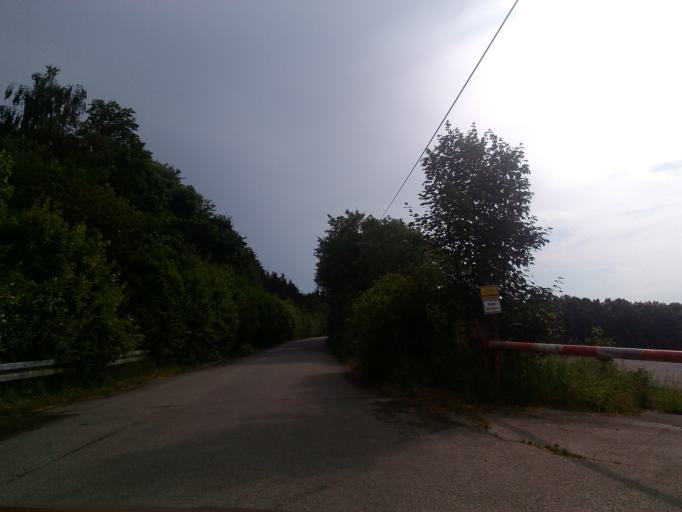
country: DE
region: Bavaria
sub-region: Upper Bavaria
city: Gilching
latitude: 48.1139
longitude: 11.2797
